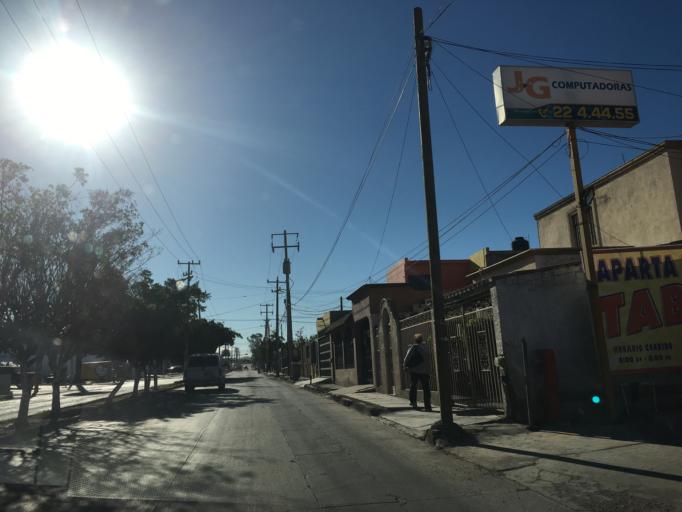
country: MX
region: Sonora
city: Heroica Guaymas
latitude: 27.9202
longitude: -110.9157
